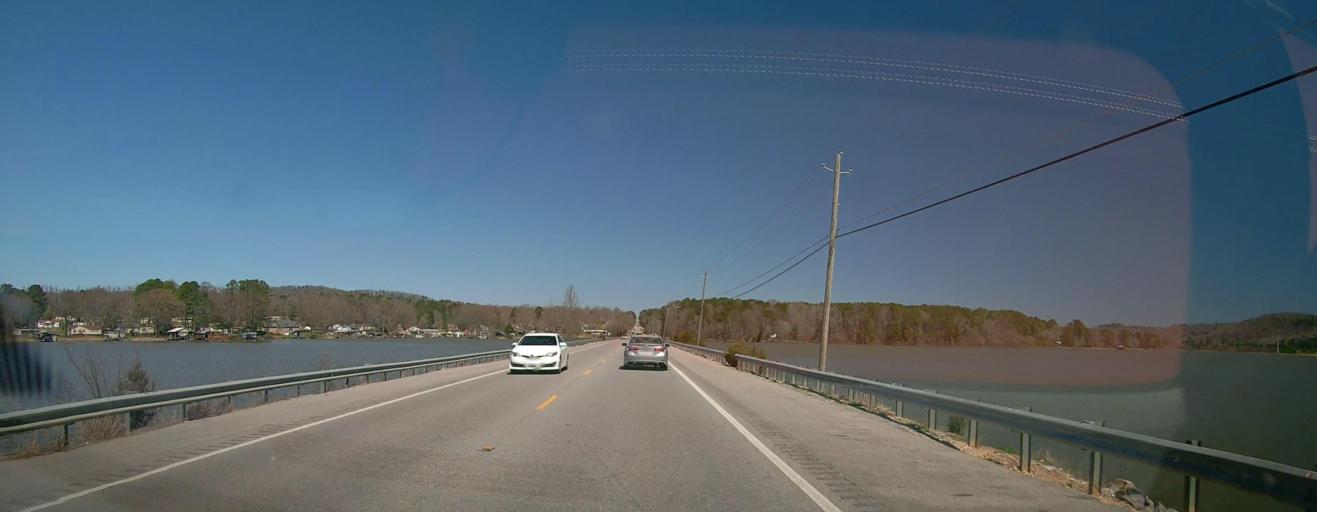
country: US
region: Alabama
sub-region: Etowah County
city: Southside
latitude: 33.8538
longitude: -86.0459
